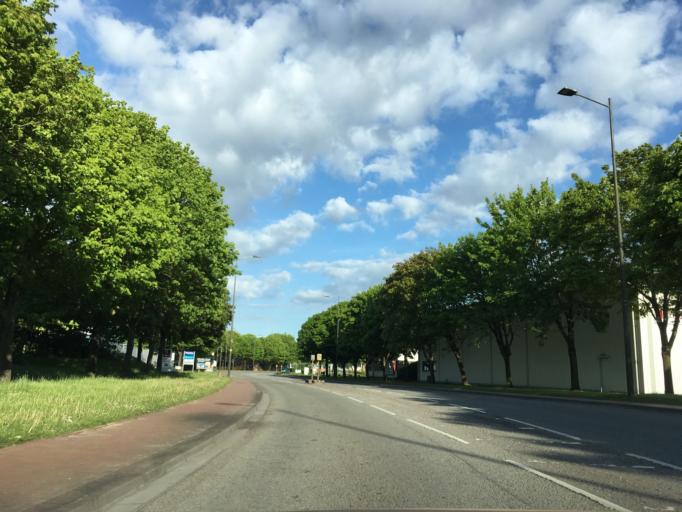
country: GB
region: Wales
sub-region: Cardiff
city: Cardiff
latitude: 51.4759
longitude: -3.1588
